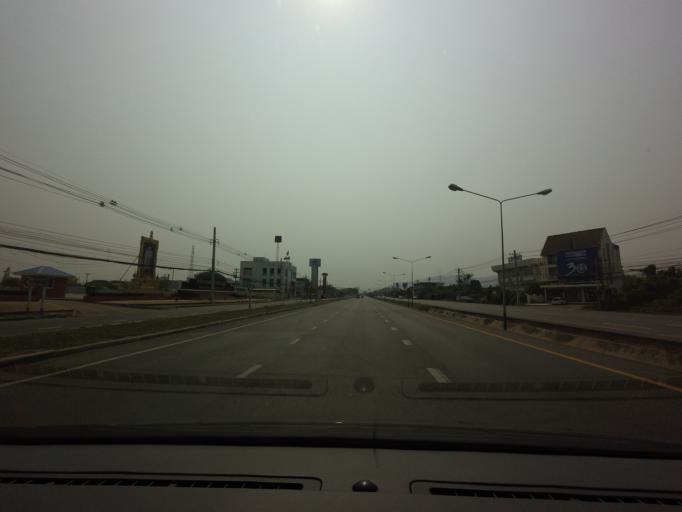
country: TH
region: Prachuap Khiri Khan
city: Pran Buri
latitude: 12.3802
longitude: 99.8927
